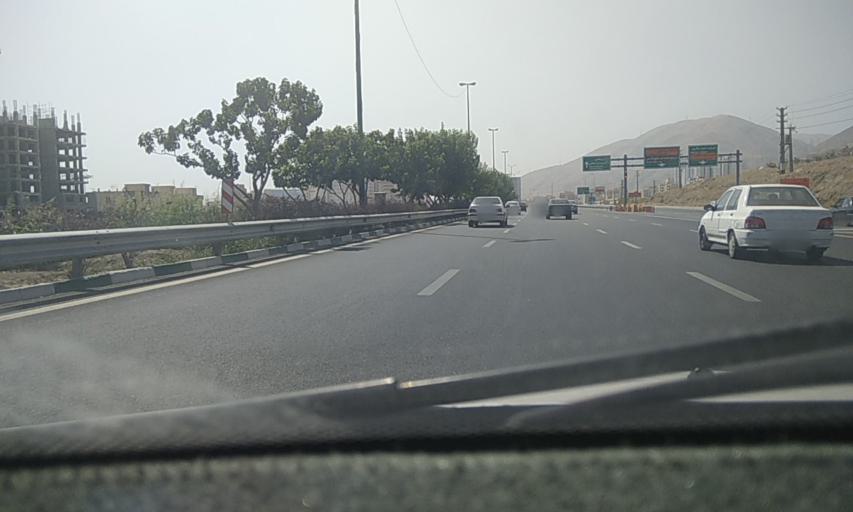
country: IR
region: Tehran
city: Shahr-e Qods
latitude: 35.7574
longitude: 51.2153
